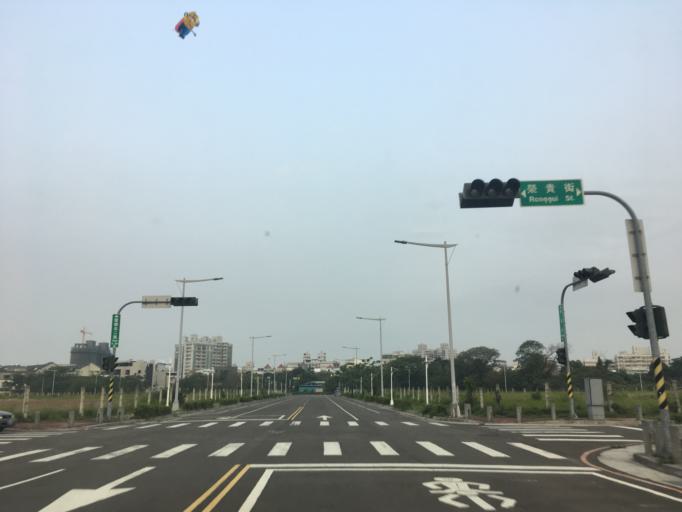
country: TW
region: Taiwan
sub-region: Taichung City
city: Taichung
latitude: 24.1967
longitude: 120.6678
